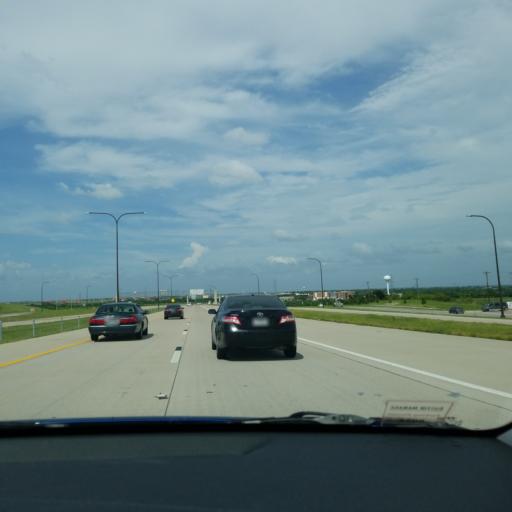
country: US
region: Texas
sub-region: Travis County
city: Manor
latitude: 30.3419
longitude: -97.5874
